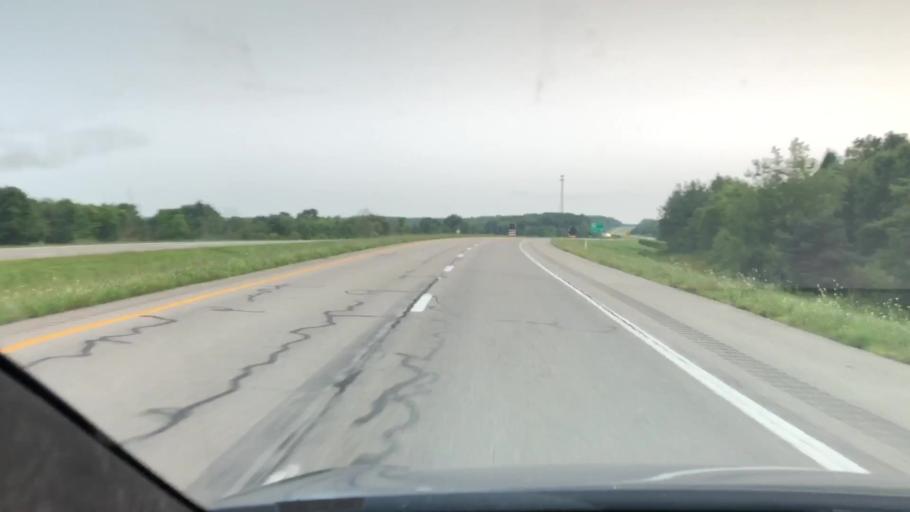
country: US
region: Pennsylvania
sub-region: Venango County
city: Franklin
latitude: 41.2715
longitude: -79.9199
